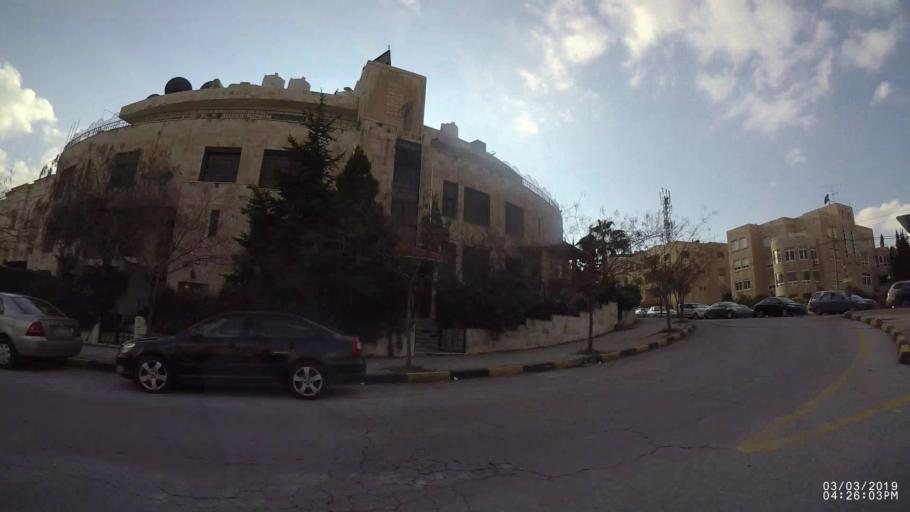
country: JO
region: Amman
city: Al Jubayhah
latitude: 31.9796
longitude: 35.8819
